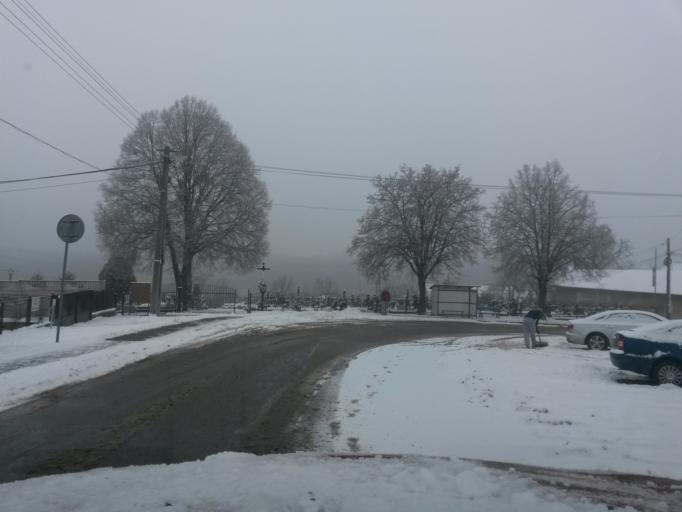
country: SK
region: Kosicky
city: Kosice
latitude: 48.7273
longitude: 21.3038
